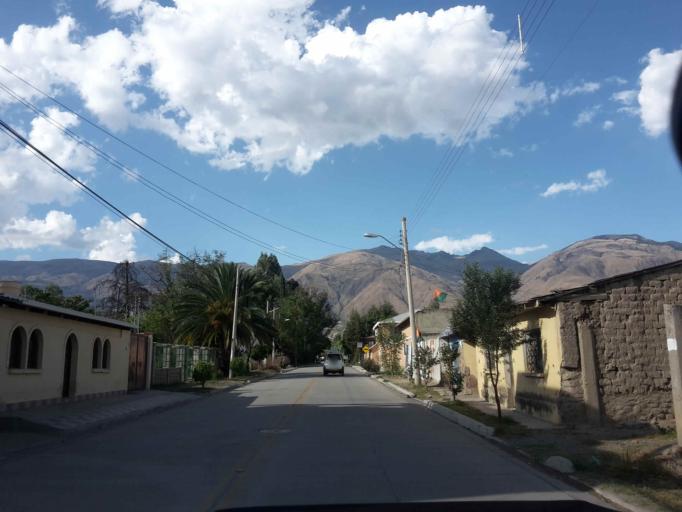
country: BO
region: Cochabamba
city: Cochabamba
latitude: -17.3598
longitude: -66.2067
